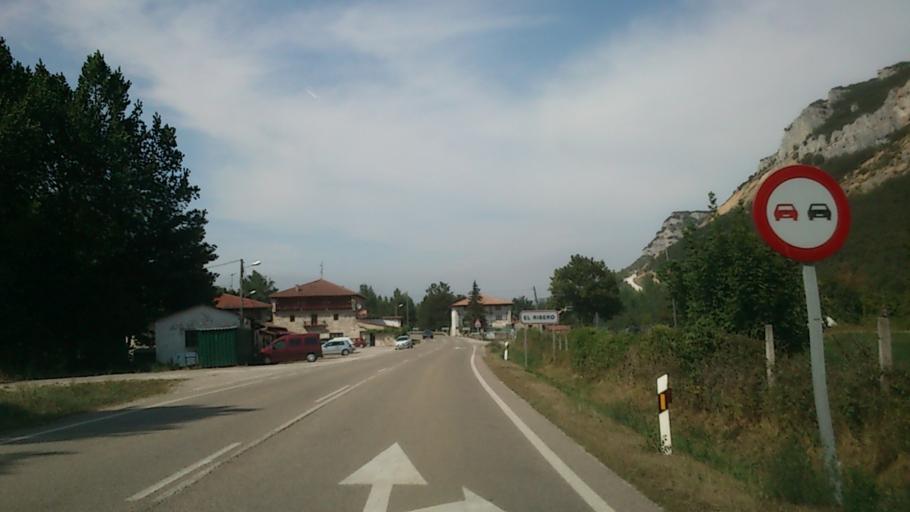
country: ES
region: Castille and Leon
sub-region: Provincia de Burgos
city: Espinosa de los Monteros
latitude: 43.0358
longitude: -3.4825
